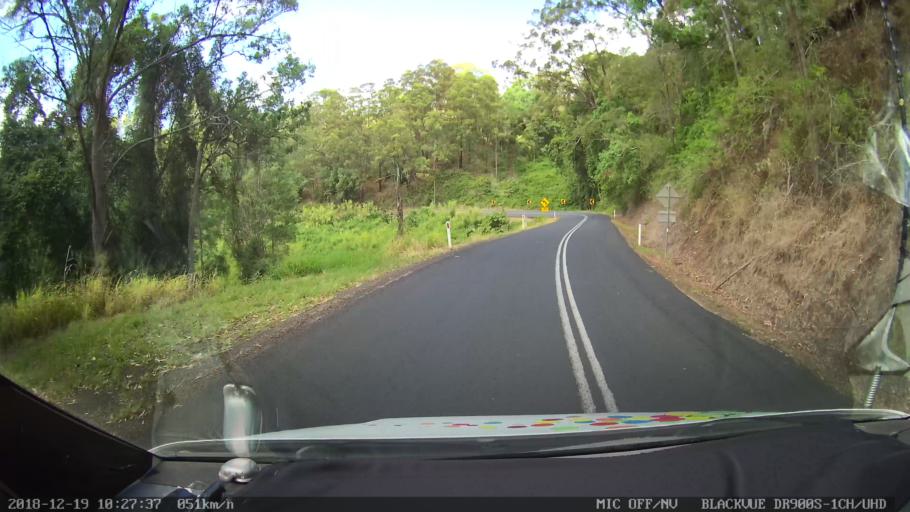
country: AU
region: New South Wales
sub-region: Lismore Municipality
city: Larnook
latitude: -28.5992
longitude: 153.0927
